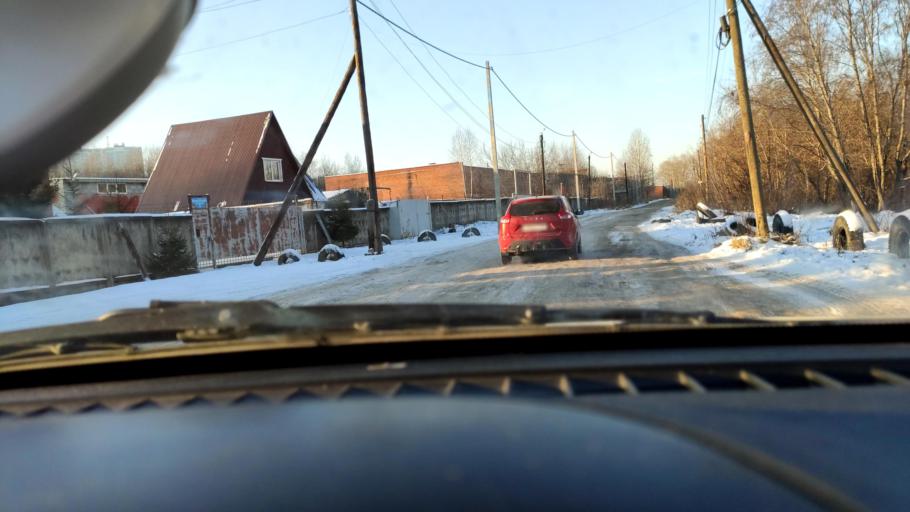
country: RU
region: Perm
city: Perm
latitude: 58.0713
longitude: 56.3629
